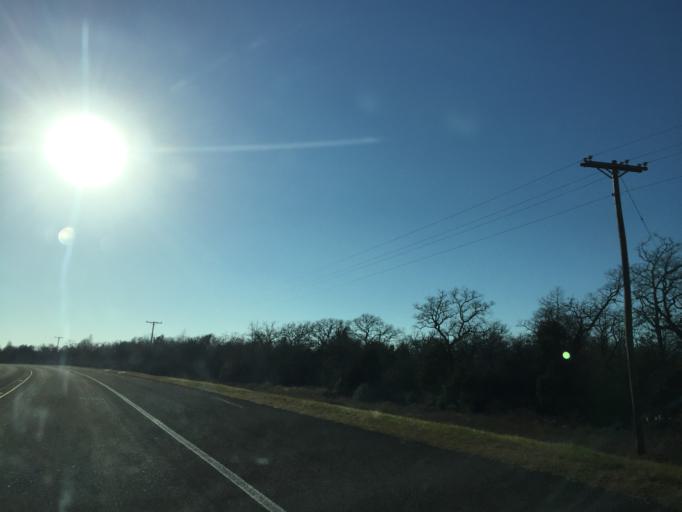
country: US
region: Texas
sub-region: Bastrop County
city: Elgin
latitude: 30.3758
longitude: -97.2570
